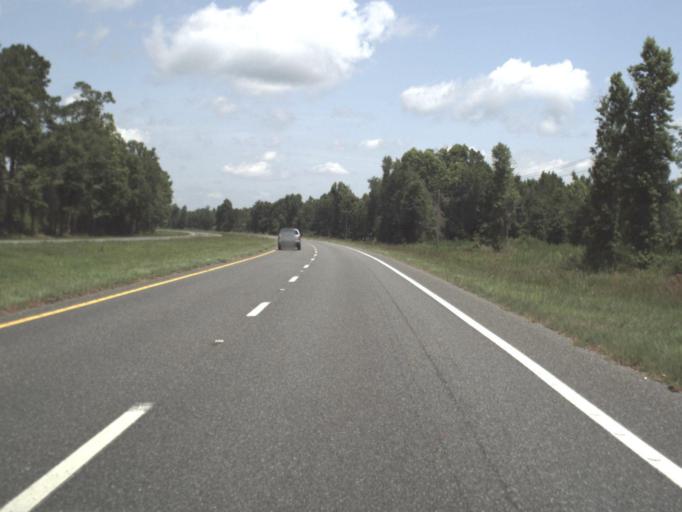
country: US
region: Florida
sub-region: Taylor County
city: Perry
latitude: 29.9439
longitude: -83.4503
